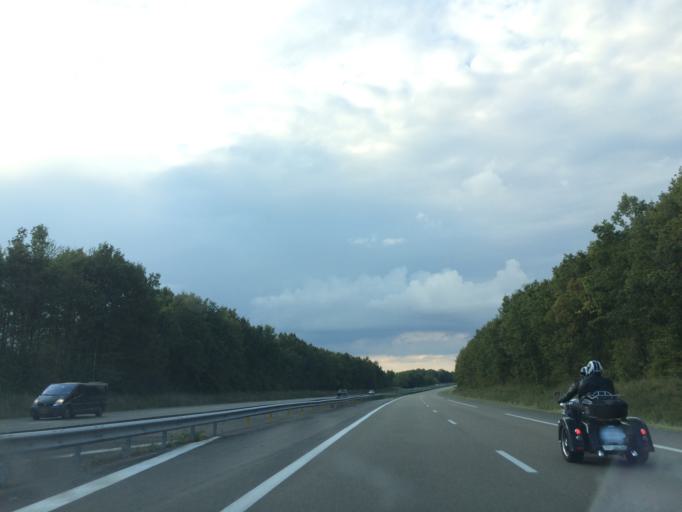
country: FR
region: Ile-de-France
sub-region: Departement de Seine-et-Marne
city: Egreville
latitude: 48.1372
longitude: 2.9202
